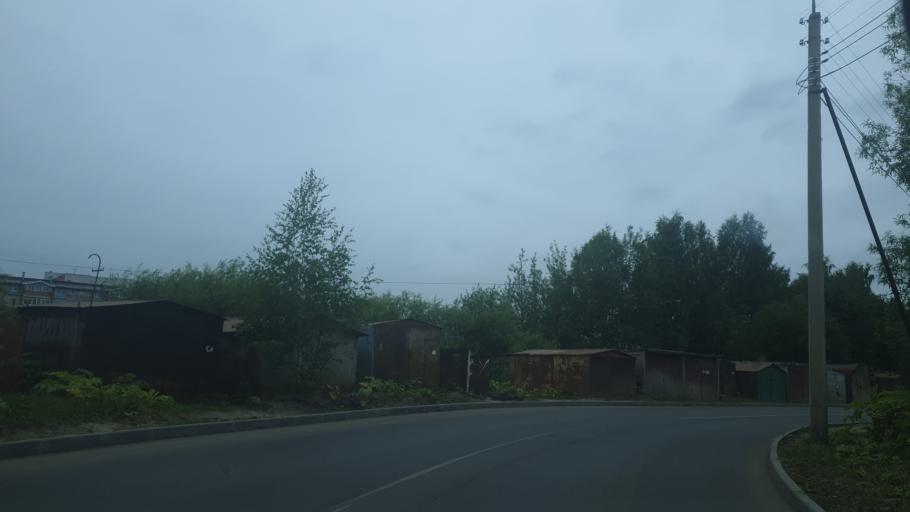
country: RU
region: Komi Republic
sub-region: Syktyvdinskiy Rayon
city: Syktyvkar
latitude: 61.6951
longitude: 50.8072
